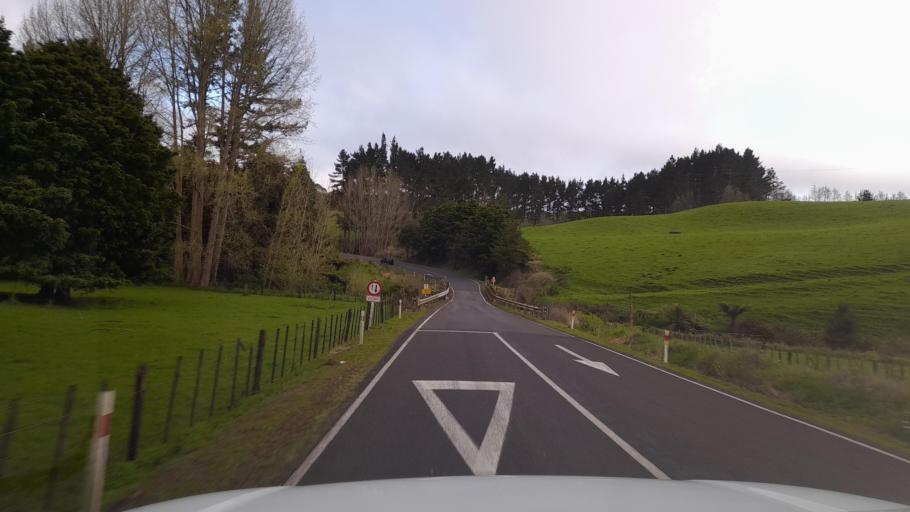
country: NZ
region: Northland
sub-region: Far North District
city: Waimate North
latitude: -35.5184
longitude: 173.8325
